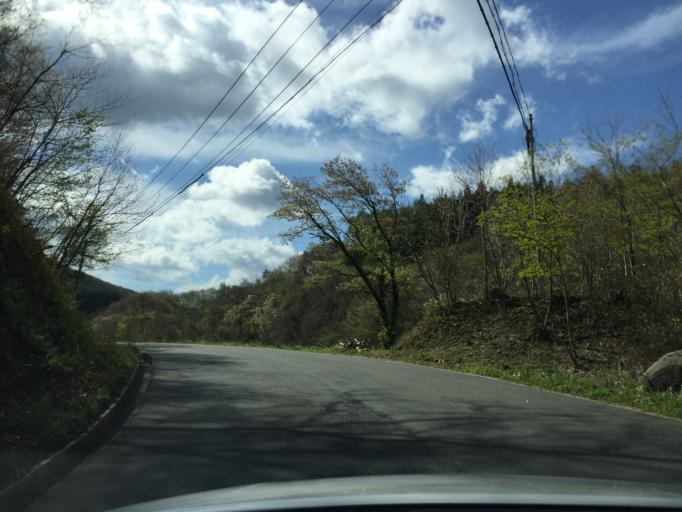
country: JP
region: Fukushima
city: Funehikimachi-funehiki
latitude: 37.5784
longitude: 140.6882
